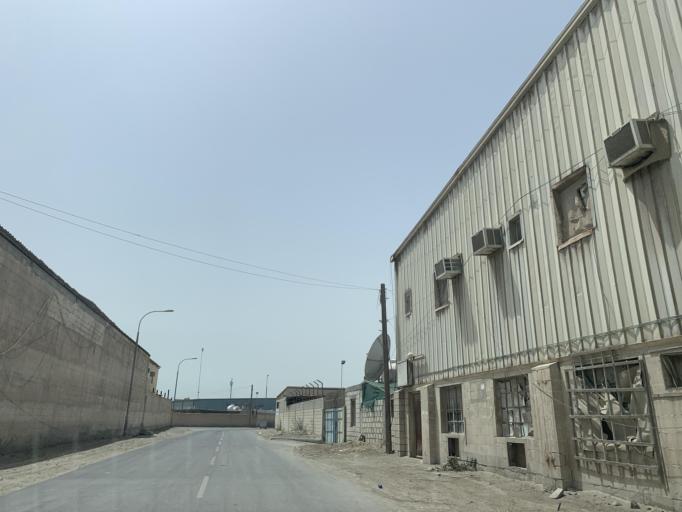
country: BH
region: Northern
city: Sitrah
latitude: 26.1452
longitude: 50.5982
